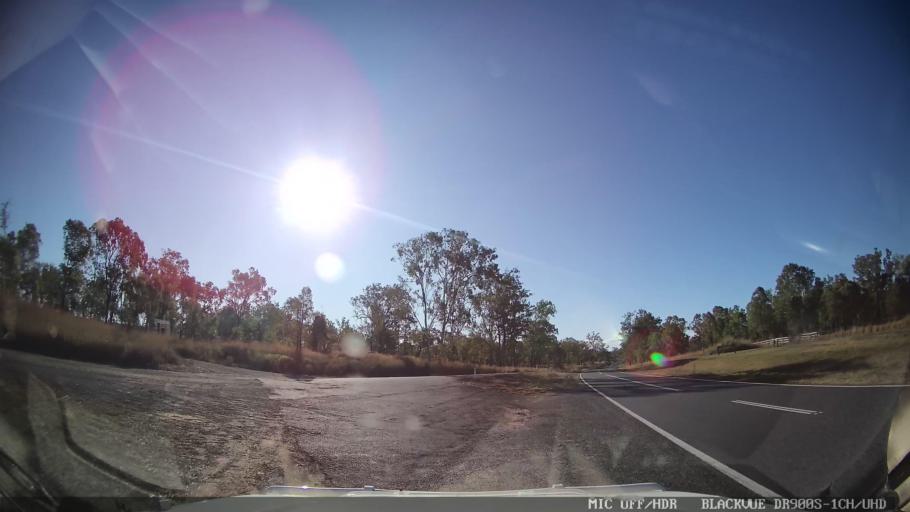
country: AU
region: Queensland
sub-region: Bundaberg
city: Sharon
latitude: -24.8241
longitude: 151.7061
